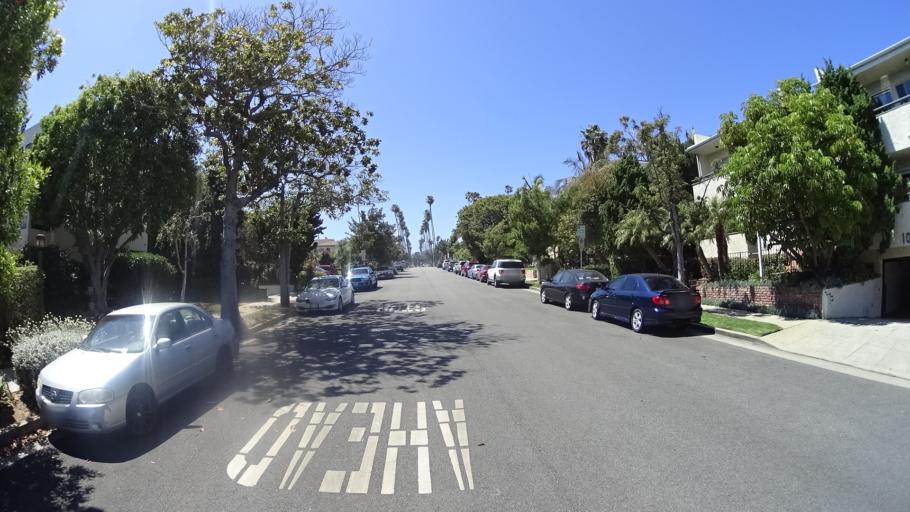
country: US
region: California
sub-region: Los Angeles County
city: Santa Monica
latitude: 34.0318
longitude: -118.4874
